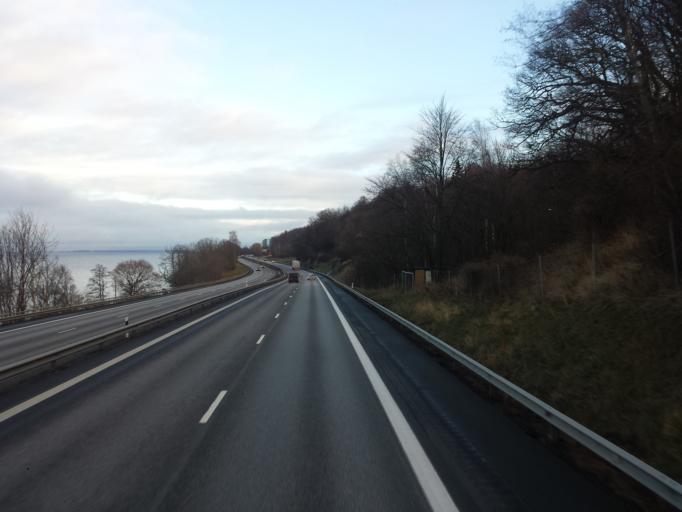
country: SE
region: Joenkoeping
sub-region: Jonkopings Kommun
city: Kaxholmen
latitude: 57.8708
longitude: 14.2727
